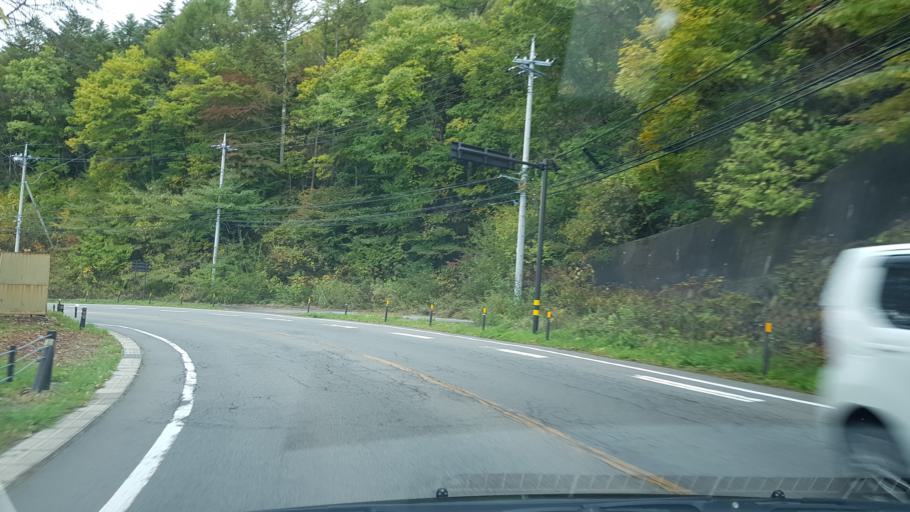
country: JP
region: Gunma
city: Nakanojomachi
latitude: 36.6073
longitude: 138.5837
